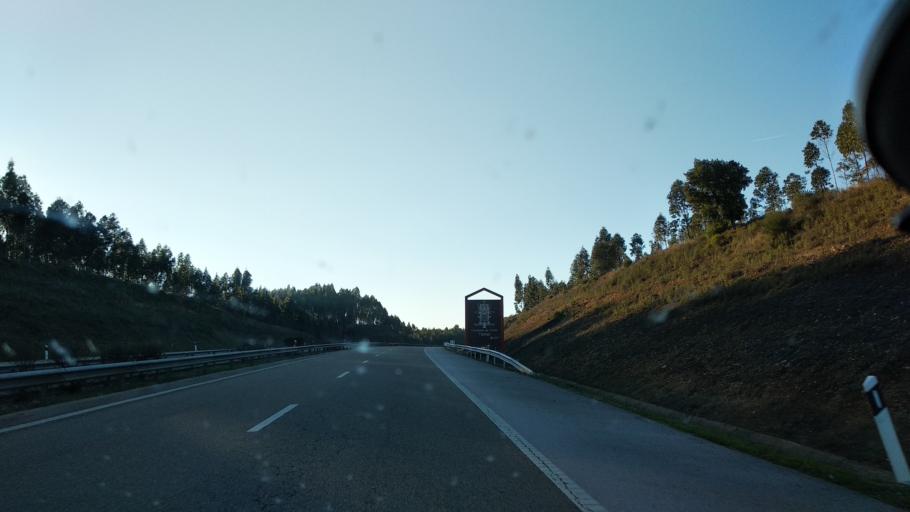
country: PT
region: Santarem
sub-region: Chamusca
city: Vila Nova da Barquinha
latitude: 39.4858
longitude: -8.4098
